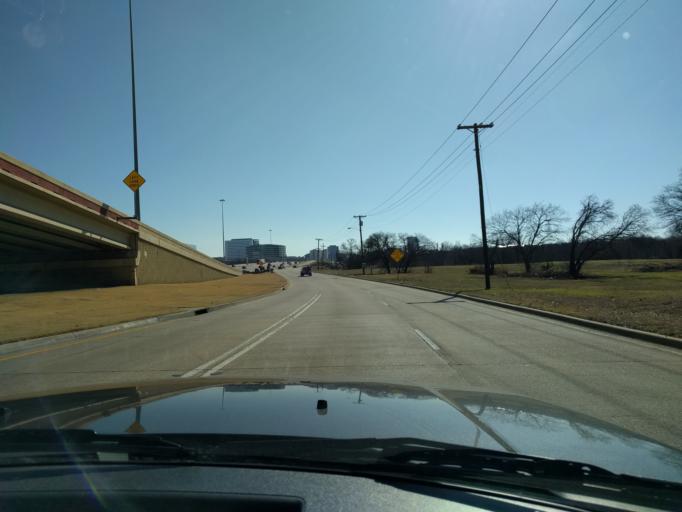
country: US
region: Texas
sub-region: Collin County
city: Plano
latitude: 33.0026
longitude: -96.7092
